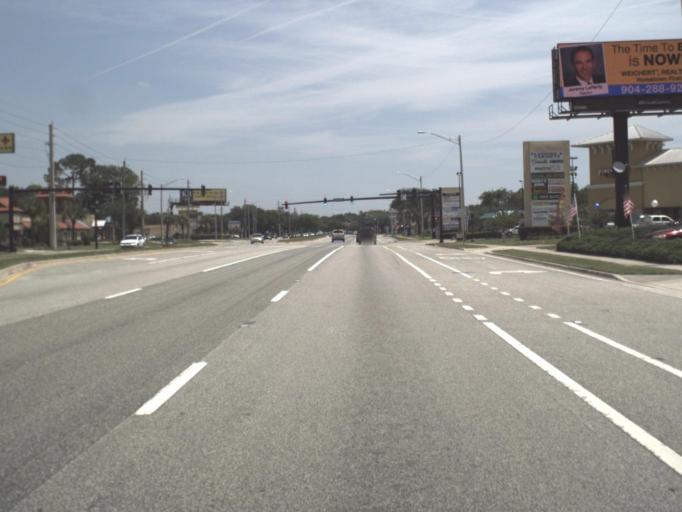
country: US
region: Florida
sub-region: Saint Johns County
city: Fruit Cove
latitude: 30.1980
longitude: -81.6208
